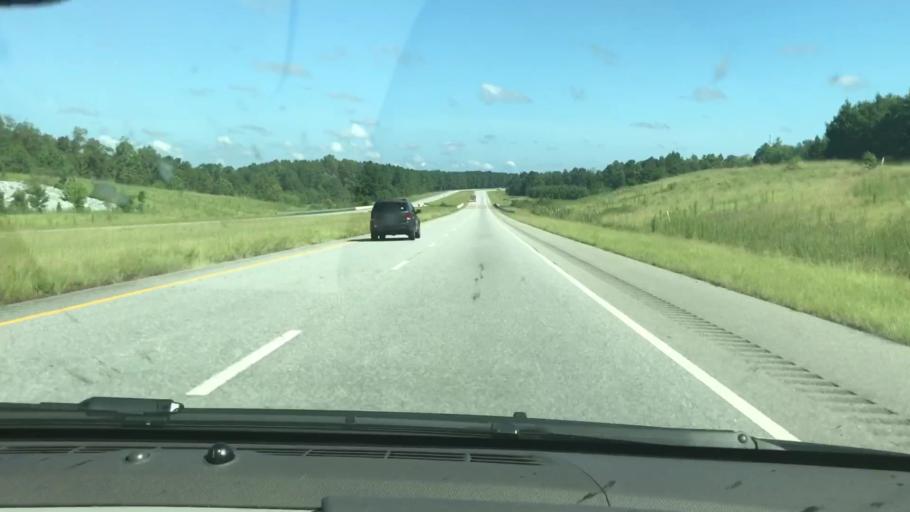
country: US
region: Alabama
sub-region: Barbour County
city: Eufaula
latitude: 32.1791
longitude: -85.1785
